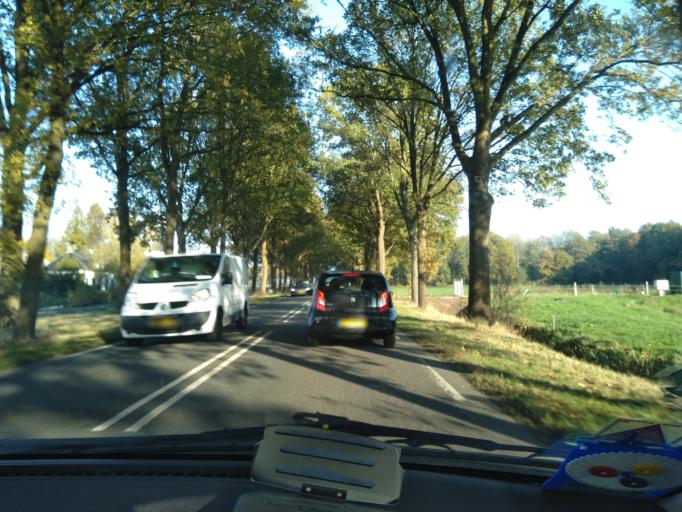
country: NL
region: Drenthe
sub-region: Gemeente Tynaarlo
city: Zuidlaren
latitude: 53.0984
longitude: 6.6946
